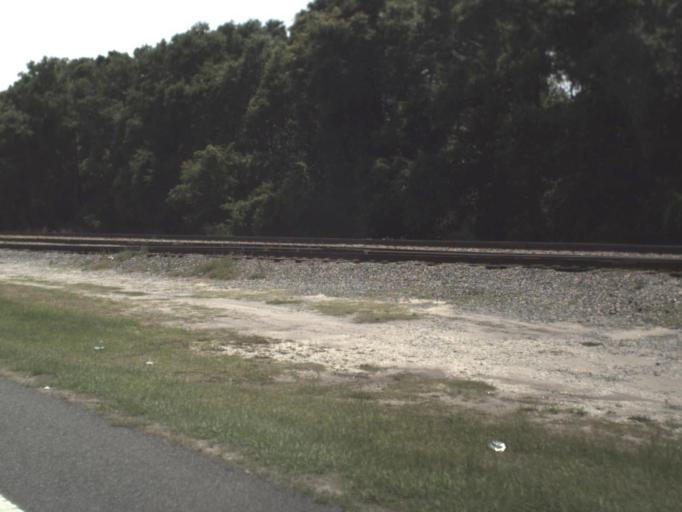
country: US
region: Florida
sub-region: Duval County
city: Jacksonville
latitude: 30.4567
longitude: -81.6362
